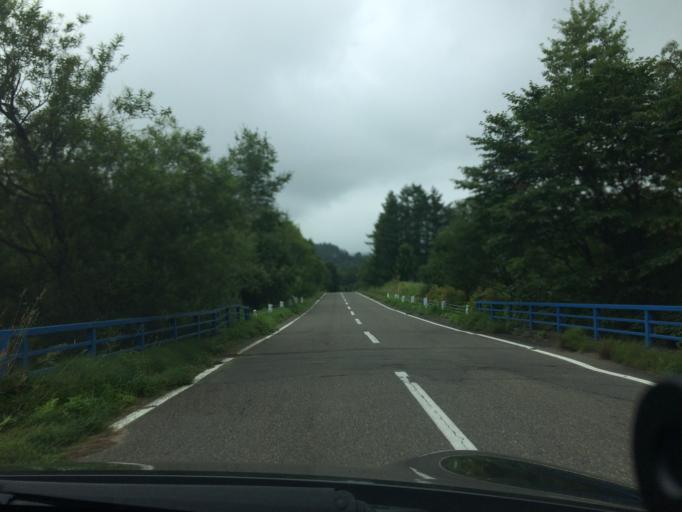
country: JP
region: Hokkaido
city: Otofuke
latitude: 42.9998
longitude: 143.0846
